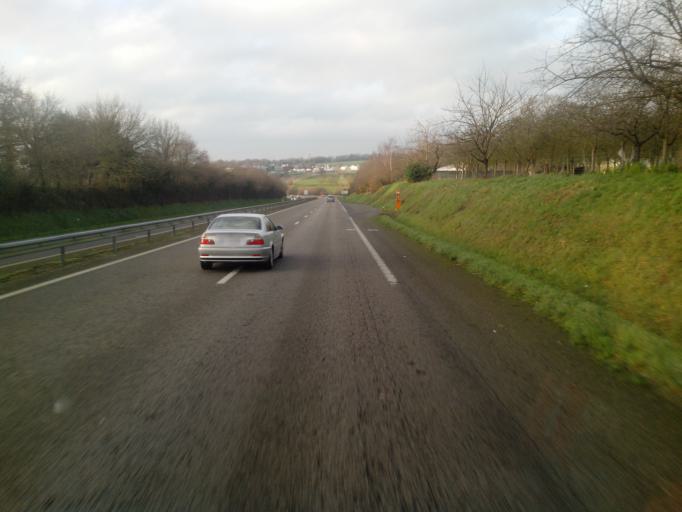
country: FR
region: Brittany
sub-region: Departement du Morbihan
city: Josselin
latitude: 47.9587
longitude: -2.5351
